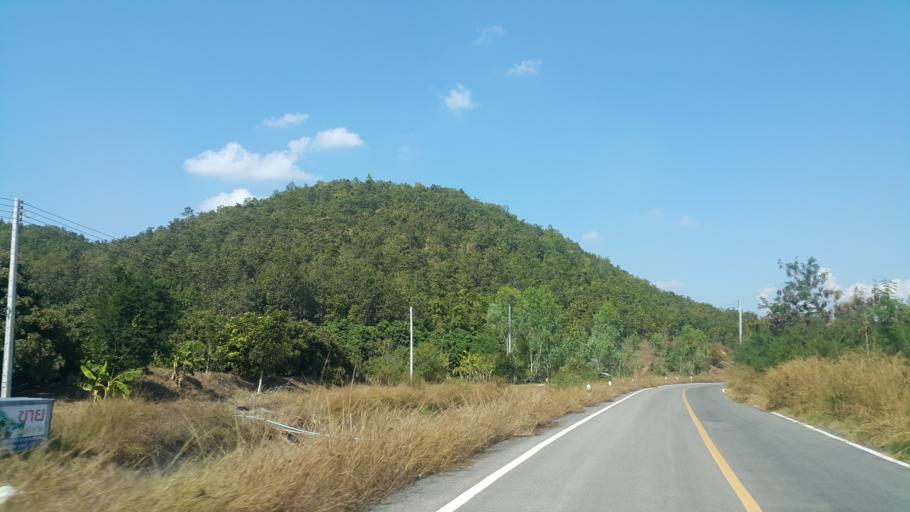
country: TH
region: Lamphun
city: Ban Thi
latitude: 18.6232
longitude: 99.1488
